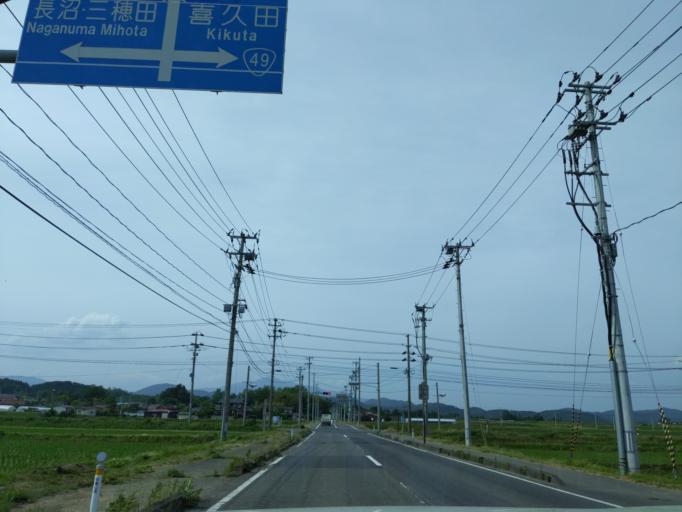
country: JP
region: Fukushima
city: Koriyama
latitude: 37.4546
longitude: 140.3128
